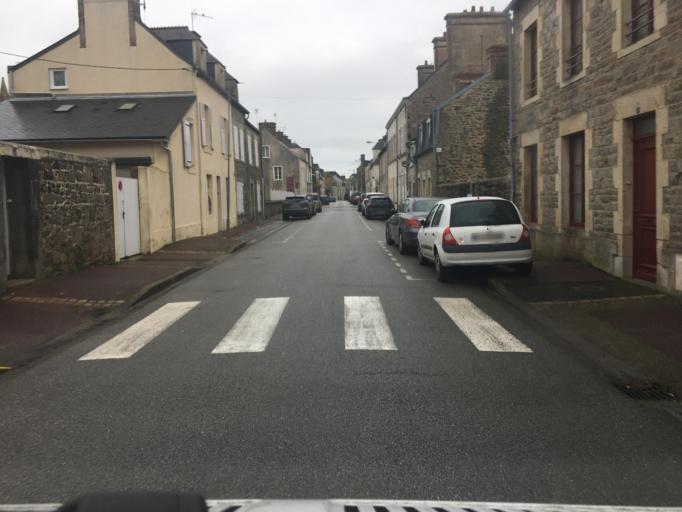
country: FR
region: Lower Normandy
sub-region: Departement de la Manche
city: Saint-Vaast-la-Hougue
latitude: 49.5869
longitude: -1.2685
